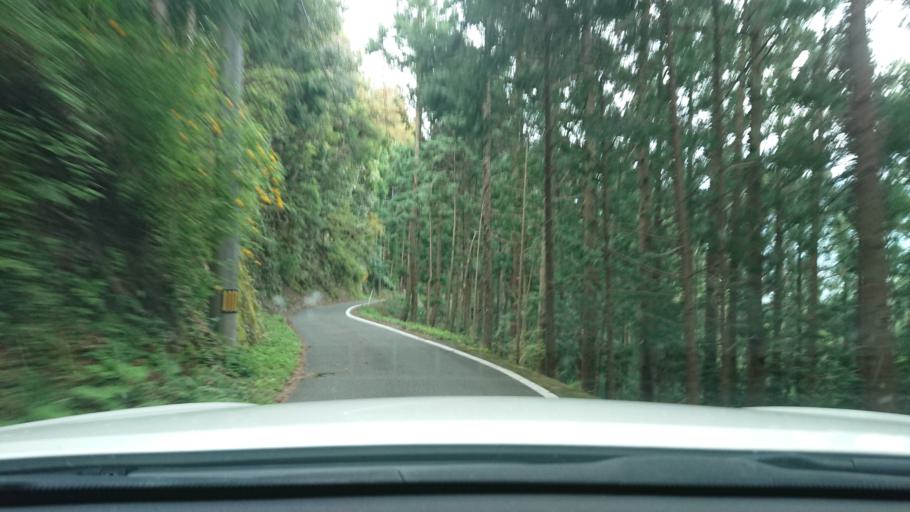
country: JP
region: Tokushima
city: Kamojimacho-jogejima
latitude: 33.8841
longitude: 134.3817
